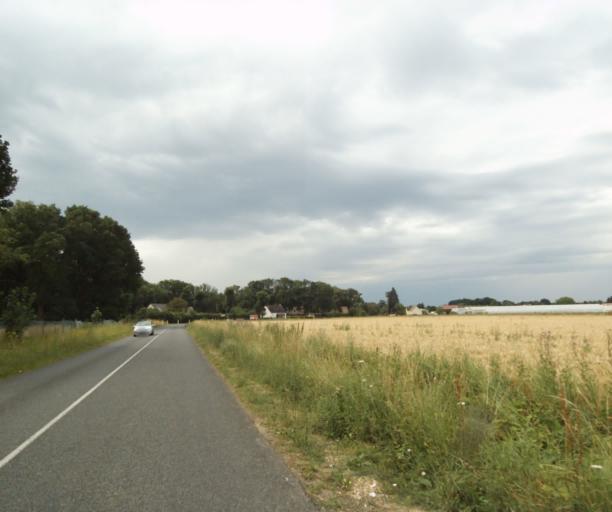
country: FR
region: Ile-de-France
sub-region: Departement de Seine-et-Marne
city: Saint-Sauveur-sur-Ecole
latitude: 48.5088
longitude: 2.5361
